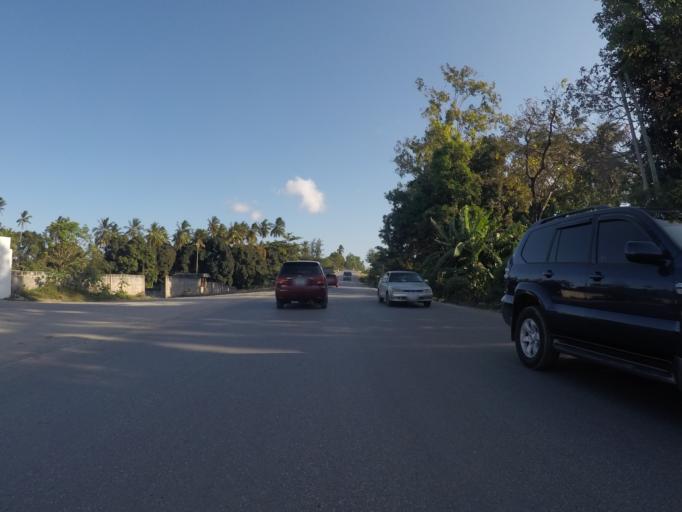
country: TZ
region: Zanzibar Urban/West
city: Zanzibar
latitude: -6.1514
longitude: 39.2360
